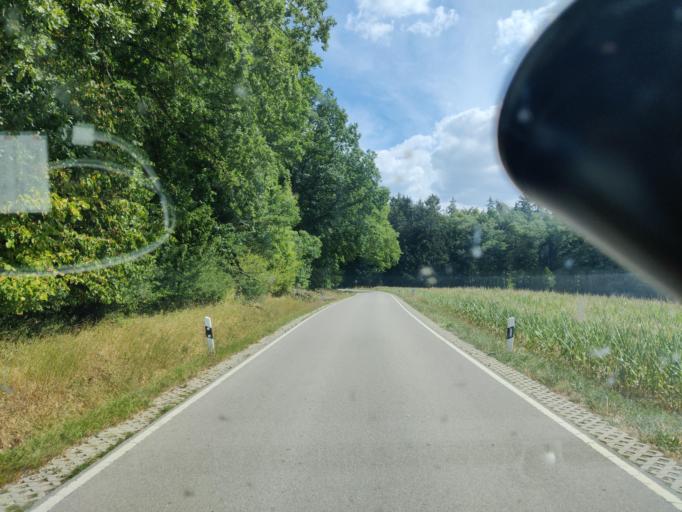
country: DE
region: Bavaria
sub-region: Regierungsbezirk Mittelfranken
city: Bergen
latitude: 49.0889
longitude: 11.1481
